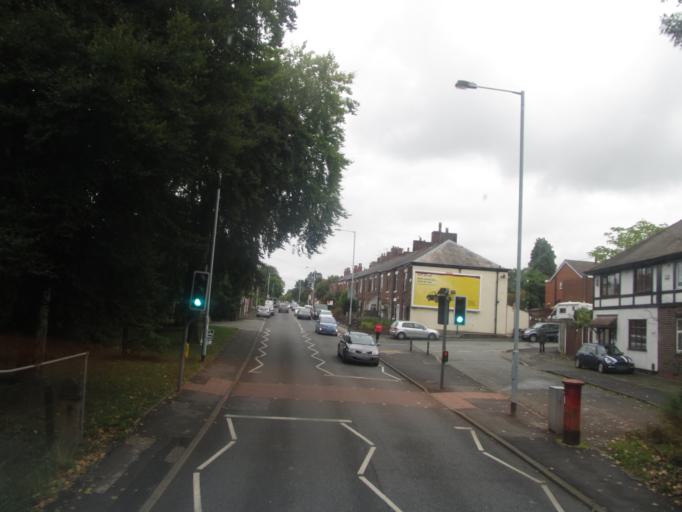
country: GB
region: England
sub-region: Borough of Tameside
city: Haughton Green
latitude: 53.4299
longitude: -2.0924
